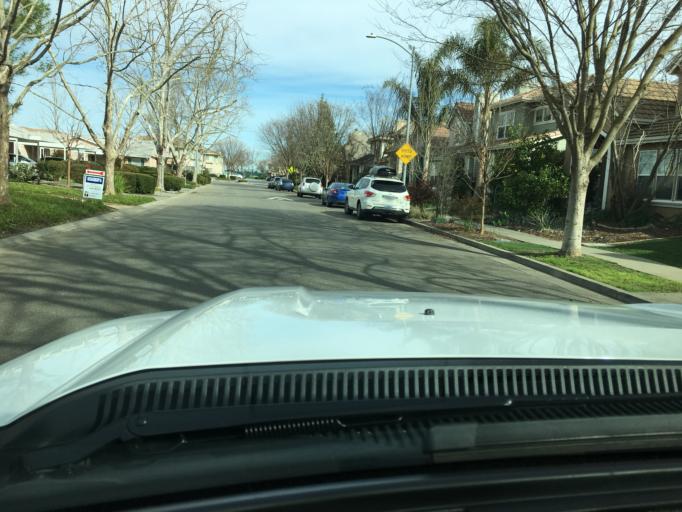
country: US
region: California
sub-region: Yolo County
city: Davis
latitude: 38.5584
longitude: -121.7763
